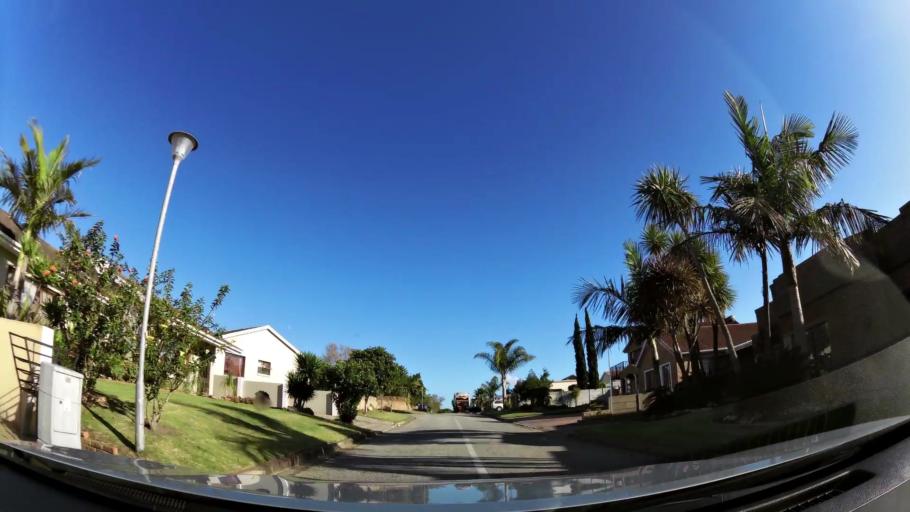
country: ZA
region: Western Cape
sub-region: Eden District Municipality
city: George
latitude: -33.9696
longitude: 22.4410
